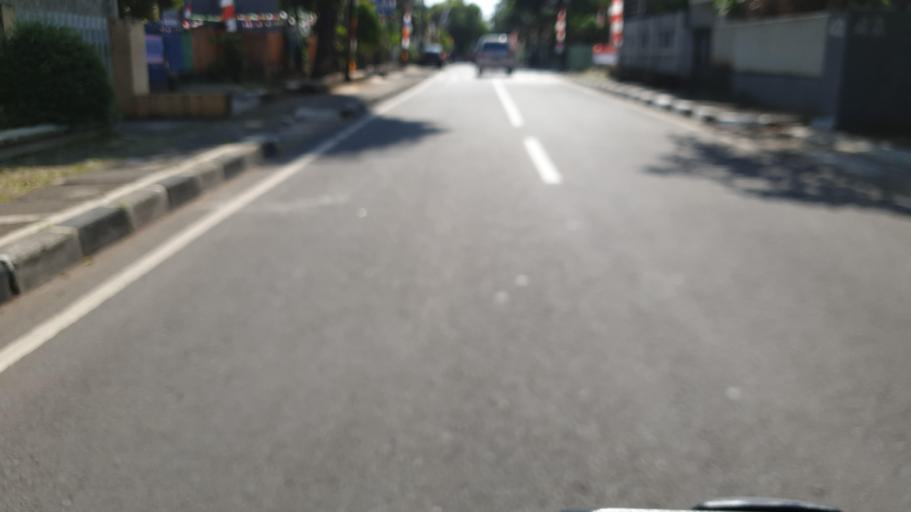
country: ID
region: Jakarta Raya
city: Jakarta
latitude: -6.2872
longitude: 106.8412
